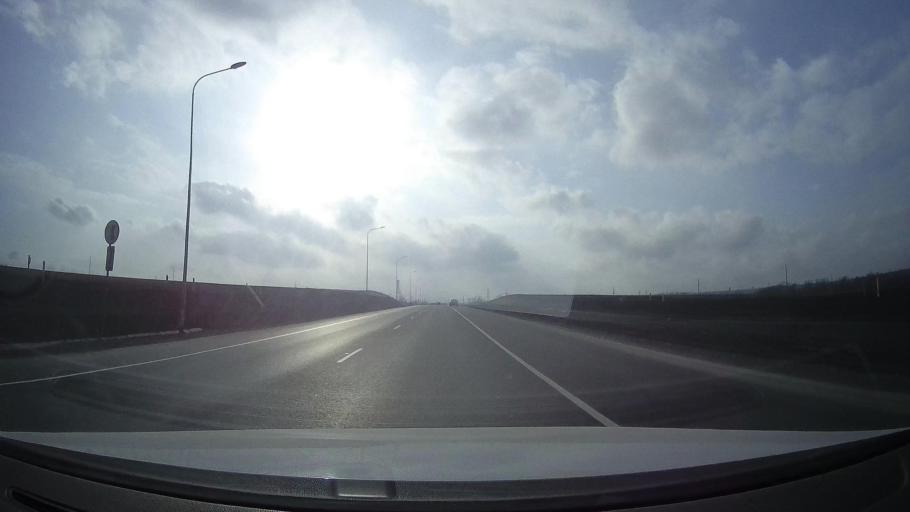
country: RU
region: Rostov
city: Grushevskaya
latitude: 47.4174
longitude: 39.8613
